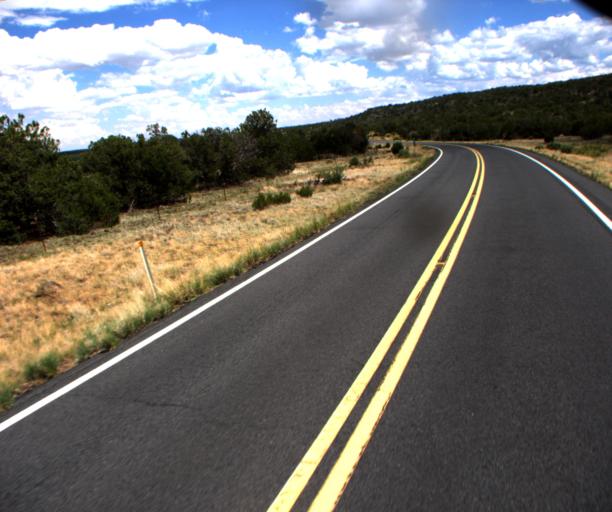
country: US
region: Arizona
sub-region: Coconino County
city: Parks
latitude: 35.5641
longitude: -111.9106
